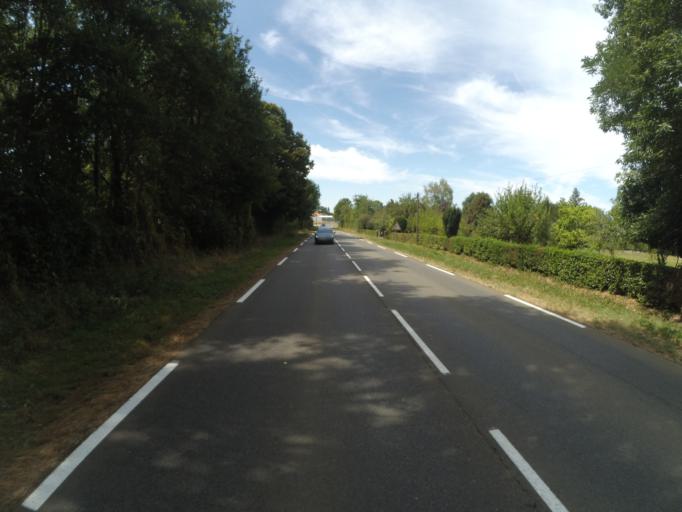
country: FR
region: Poitou-Charentes
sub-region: Departement de la Charente
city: Confolens
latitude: 45.9575
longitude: 0.7040
